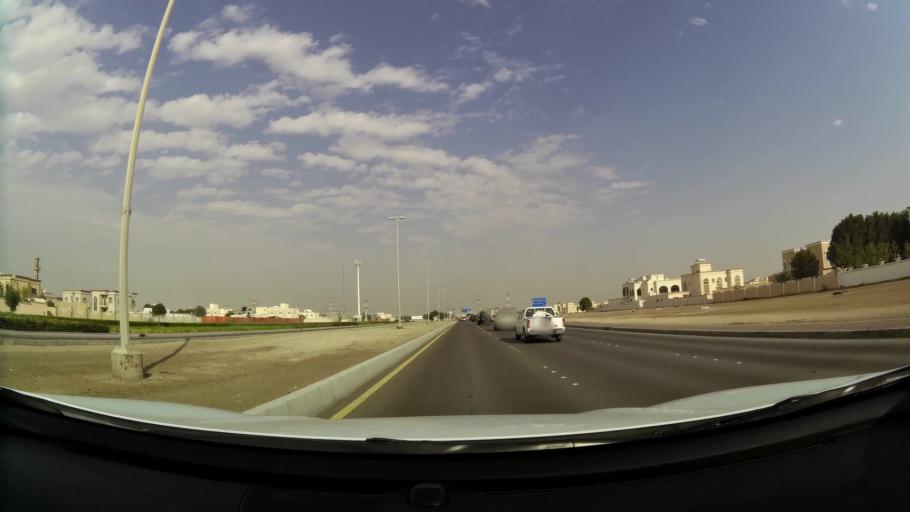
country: AE
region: Abu Dhabi
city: Abu Dhabi
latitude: 24.3259
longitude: 54.5716
